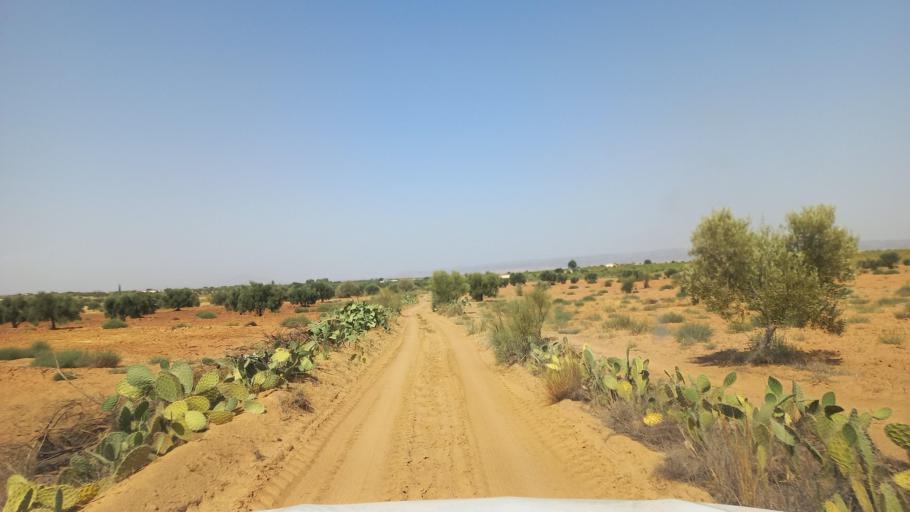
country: TN
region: Al Qasrayn
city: Kasserine
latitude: 35.2404
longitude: 9.0634
